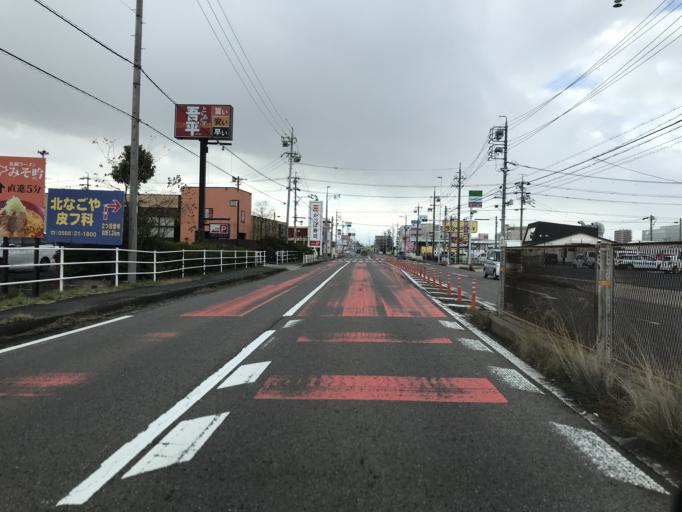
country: JP
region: Aichi
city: Iwakura
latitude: 35.2417
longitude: 136.8816
